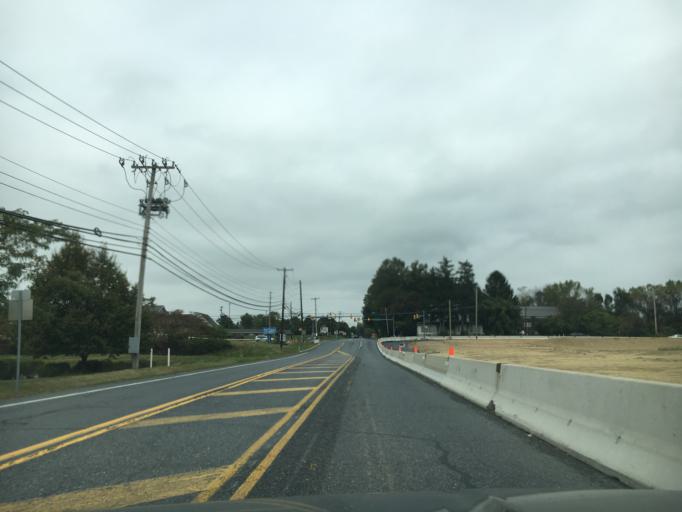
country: US
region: Pennsylvania
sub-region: Northampton County
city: Bath
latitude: 40.7025
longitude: -75.4179
